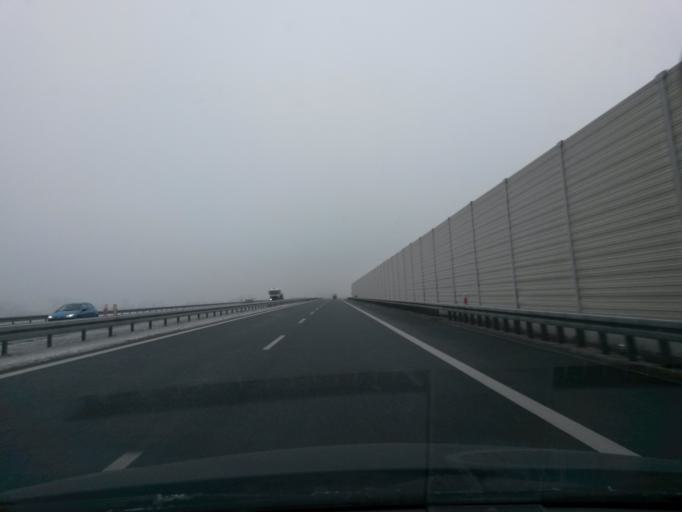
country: PL
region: Greater Poland Voivodeship
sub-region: Powiat gnieznienski
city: Lubowo
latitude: 52.4948
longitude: 17.4485
